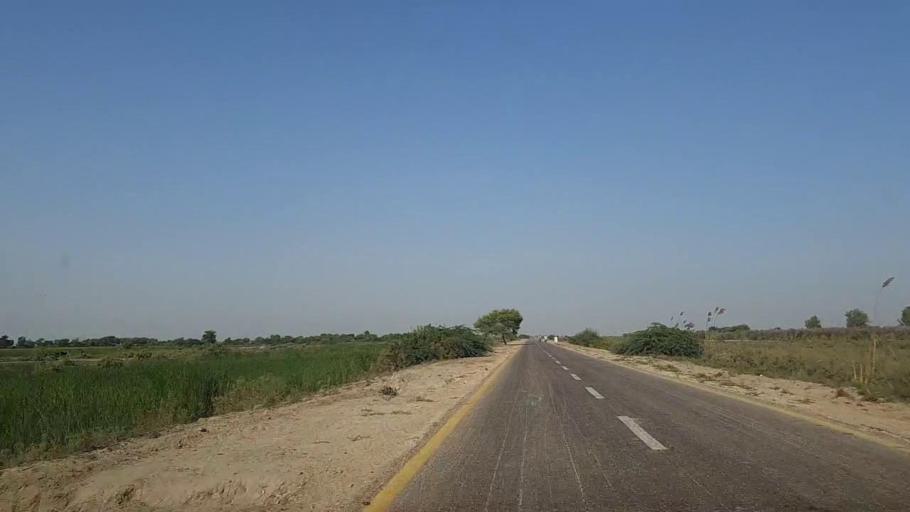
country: PK
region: Sindh
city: Jati
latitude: 24.3901
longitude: 68.2870
